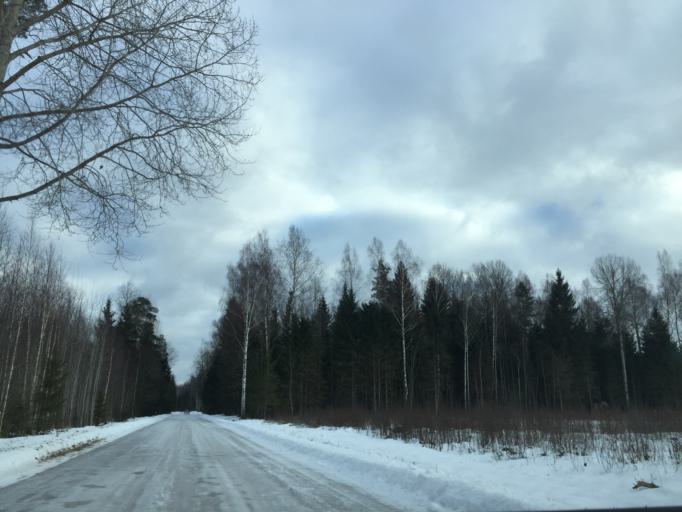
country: LV
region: Lielvarde
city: Lielvarde
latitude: 56.5835
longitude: 24.7427
